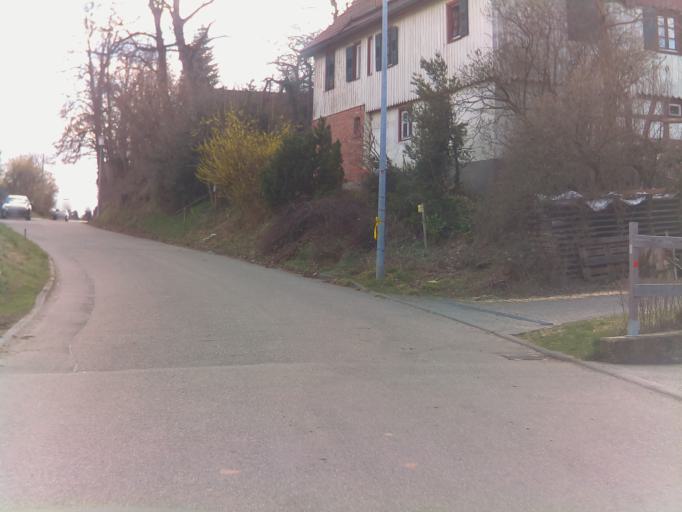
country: DE
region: Baden-Wuerttemberg
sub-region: Regierungsbezirk Stuttgart
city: Alfdorf
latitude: 48.8412
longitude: 9.6788
